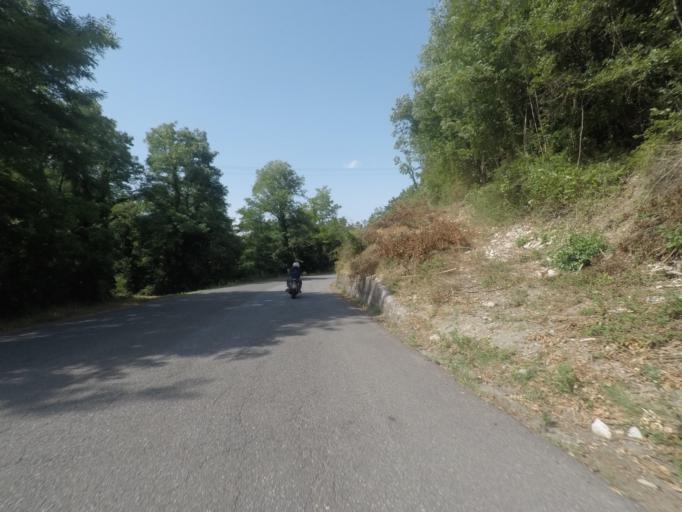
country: IT
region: Tuscany
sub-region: Provincia di Massa-Carrara
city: Fivizzano
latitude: 44.1717
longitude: 10.1151
